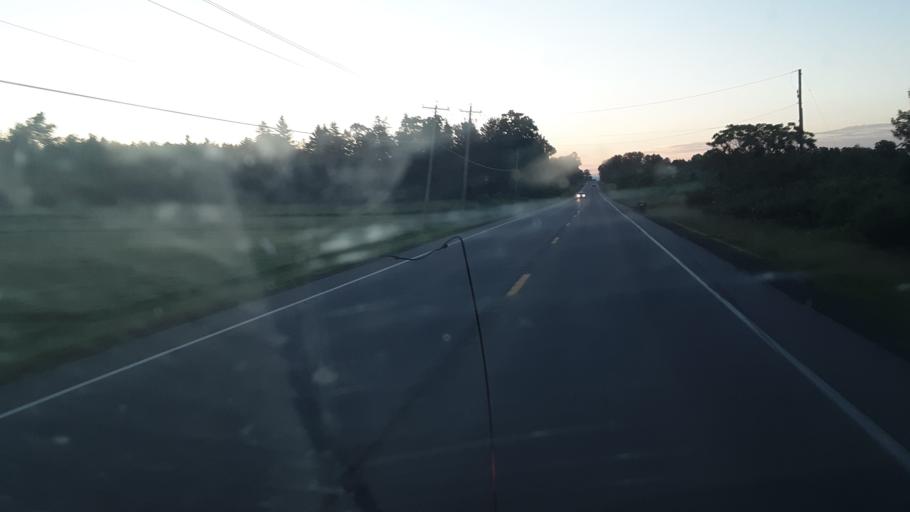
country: US
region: New York
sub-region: Schenectady County
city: East Glenville
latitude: 42.9746
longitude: -74.0059
